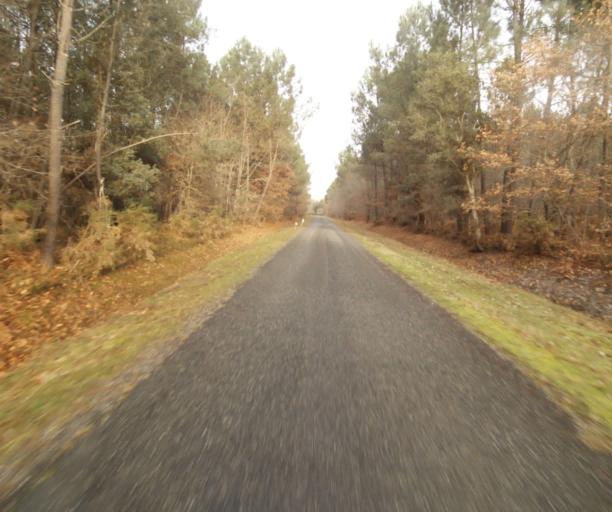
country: FR
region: Aquitaine
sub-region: Departement des Landes
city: Gabarret
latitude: 44.0906
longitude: 0.0666
